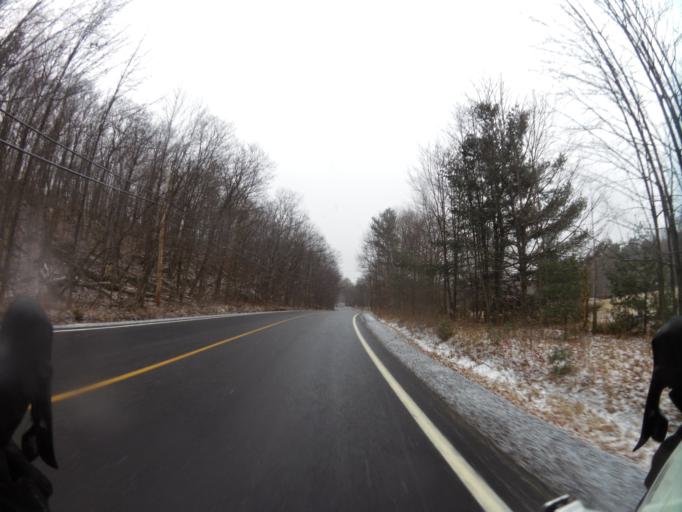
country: CA
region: Quebec
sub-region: Outaouais
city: Gatineau
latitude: 45.4986
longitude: -75.8211
